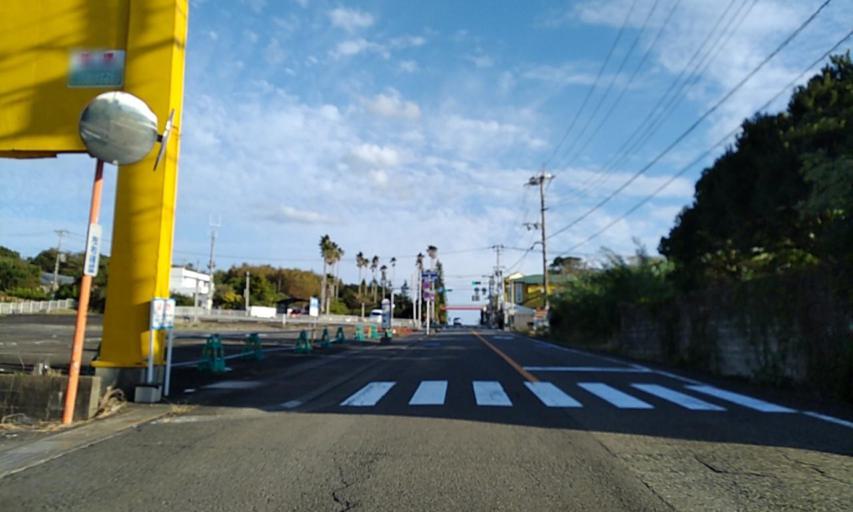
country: JP
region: Wakayama
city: Tanabe
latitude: 33.6669
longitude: 135.3361
